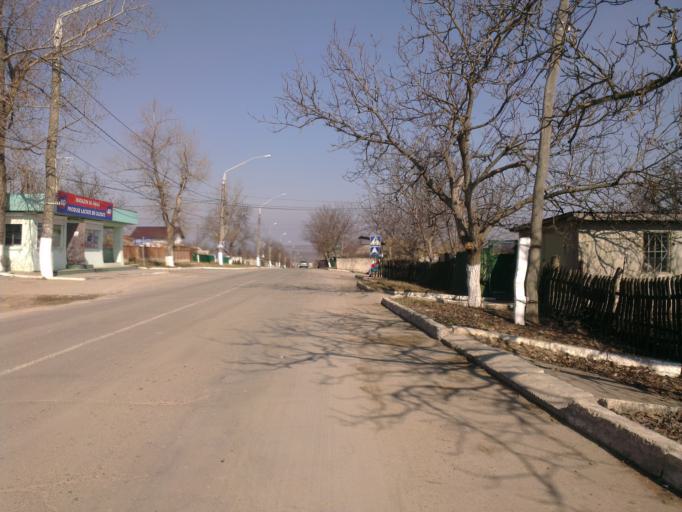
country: MD
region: Chisinau
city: Cricova
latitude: 47.1296
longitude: 28.8651
